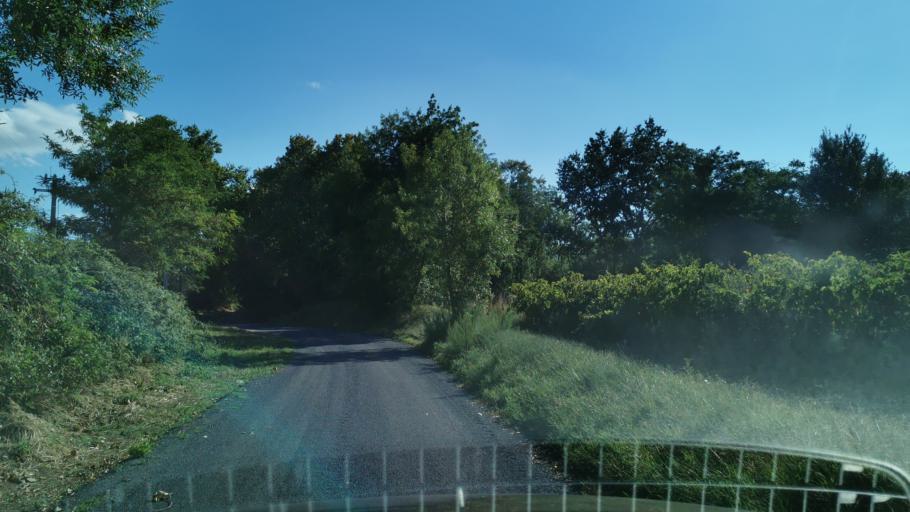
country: FR
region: Languedoc-Roussillon
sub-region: Departement de l'Aude
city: Ginestas
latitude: 43.2436
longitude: 2.8812
